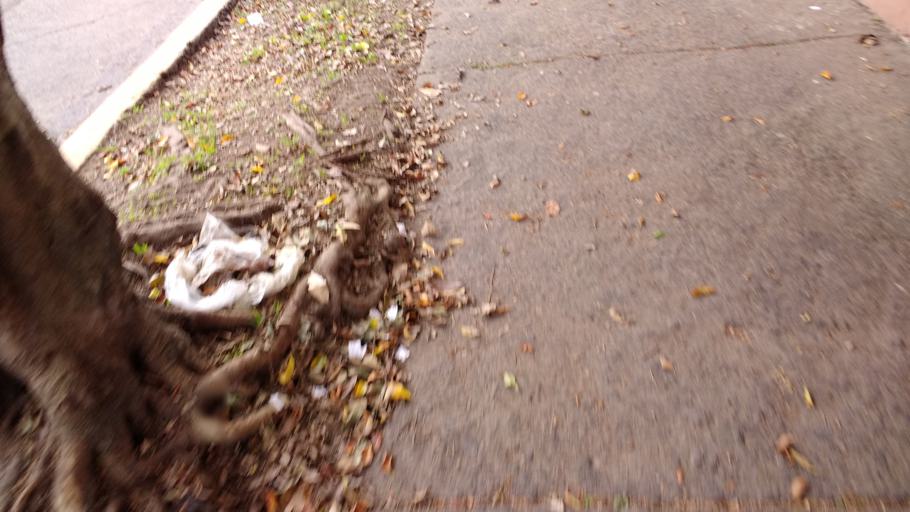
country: MX
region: Veracruz
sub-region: Xalapa
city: Xalapa de Enriquez
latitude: 19.5347
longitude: -96.9167
